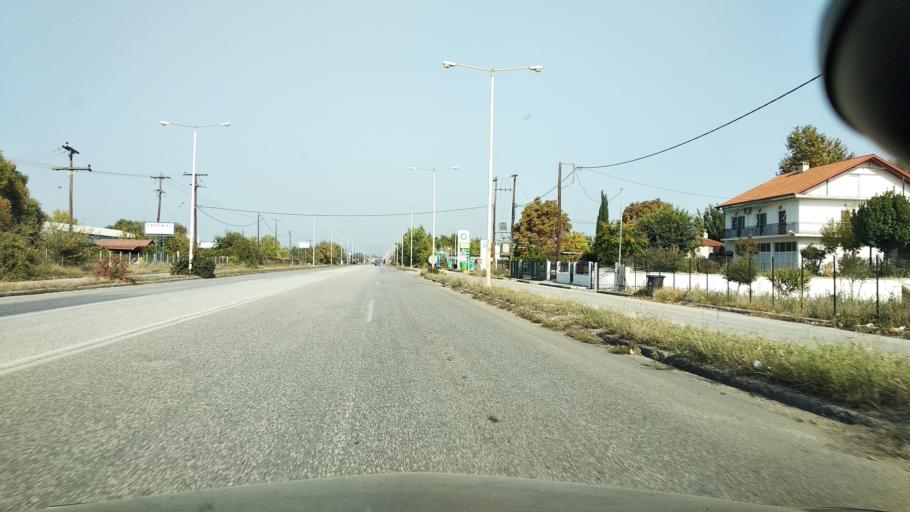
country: GR
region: Thessaly
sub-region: Trikala
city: Pyrgetos
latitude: 39.5769
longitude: 21.7442
